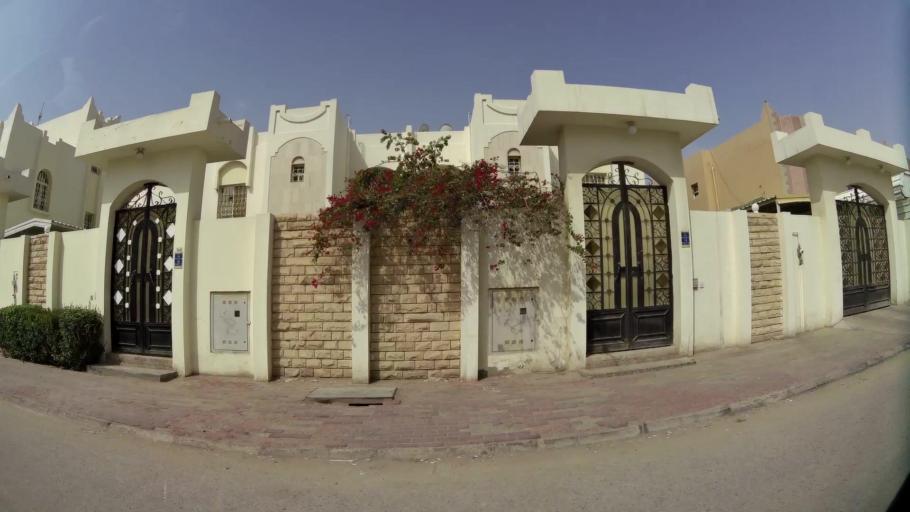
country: QA
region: Baladiyat ad Dawhah
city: Doha
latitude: 25.3058
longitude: 51.4761
